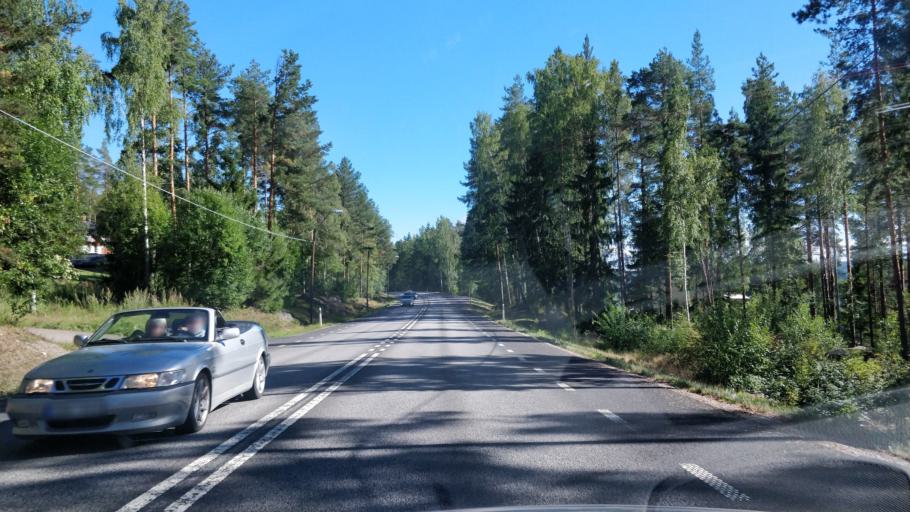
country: SE
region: Dalarna
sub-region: Faluns Kommun
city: Grycksbo
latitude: 60.6923
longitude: 15.4868
